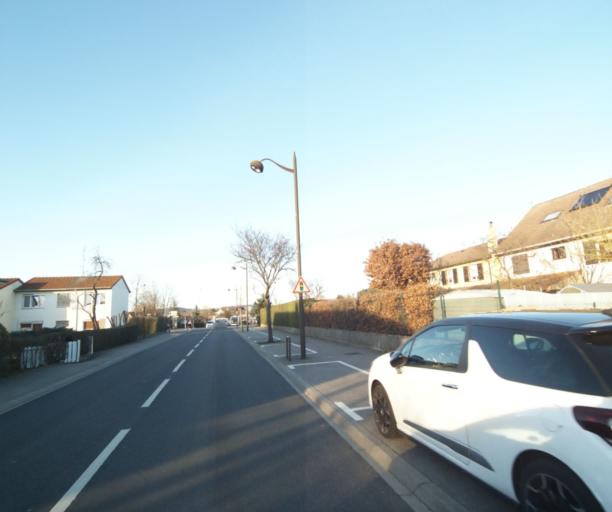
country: FR
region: Lorraine
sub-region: Departement de Meurthe-et-Moselle
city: Pulnoy
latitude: 48.7049
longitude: 6.2605
